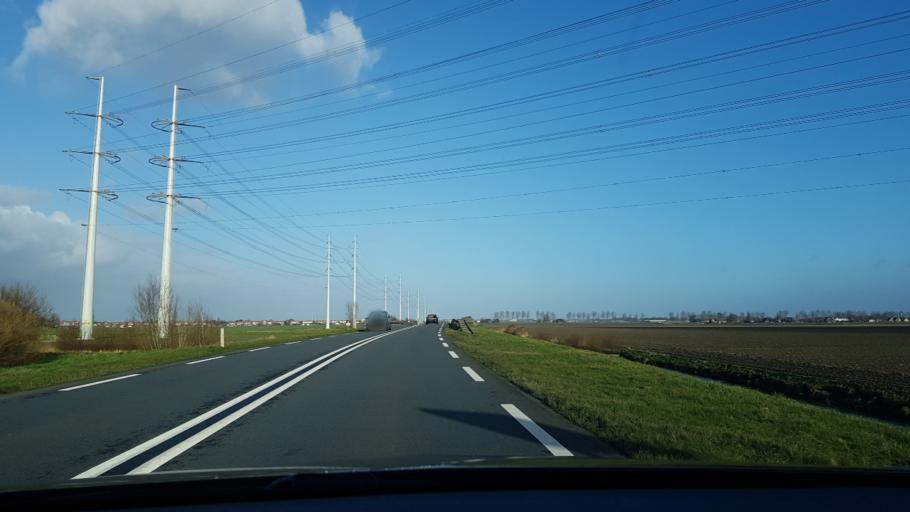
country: NL
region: South Holland
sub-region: Gemeente Hillegom
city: Hillegom
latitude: 52.2729
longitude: 4.5888
